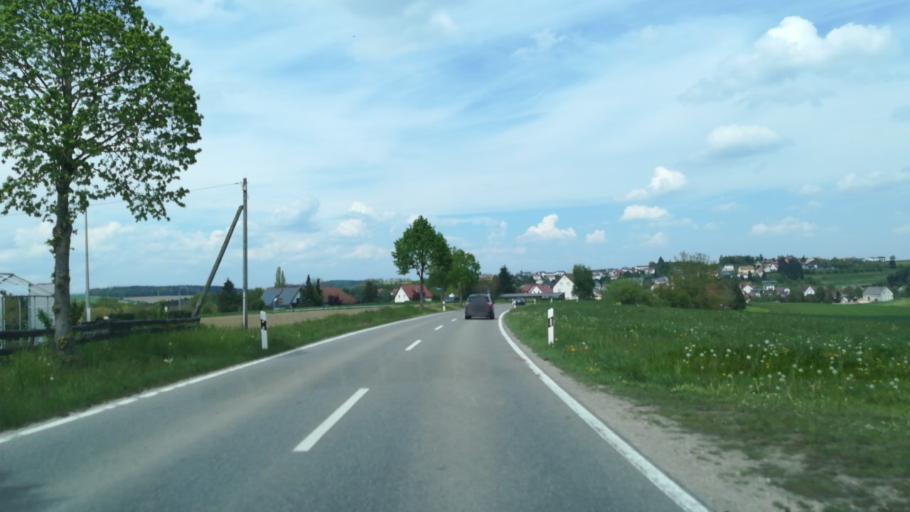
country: DE
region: Baden-Wuerttemberg
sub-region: Freiburg Region
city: Muhlingen
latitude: 47.8914
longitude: 9.0349
